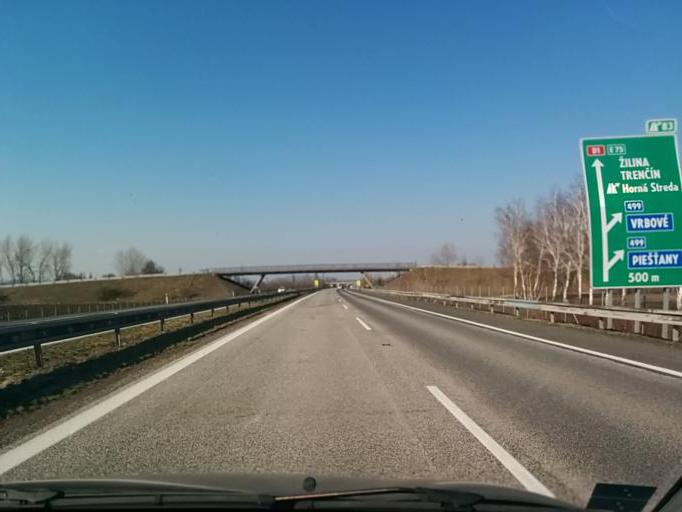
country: SK
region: Trnavsky
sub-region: Okres Trnava
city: Piestany
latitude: 48.5813
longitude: 17.7897
